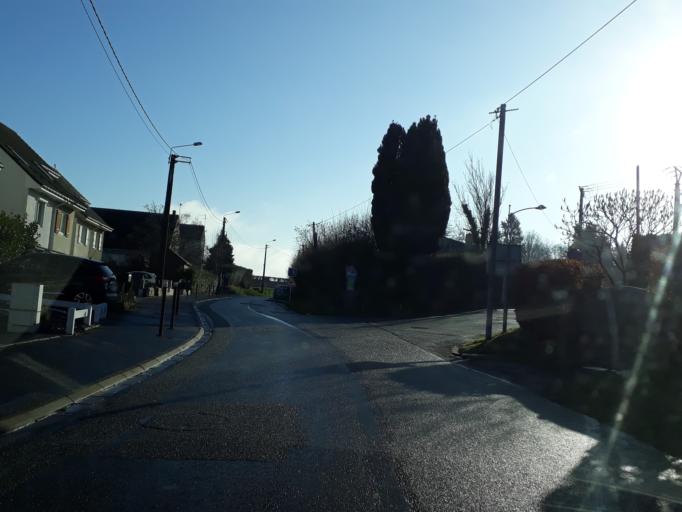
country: FR
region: Nord-Pas-de-Calais
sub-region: Departement du Nord
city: Wargnies-le-Grand
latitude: 50.3087
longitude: 3.6642
